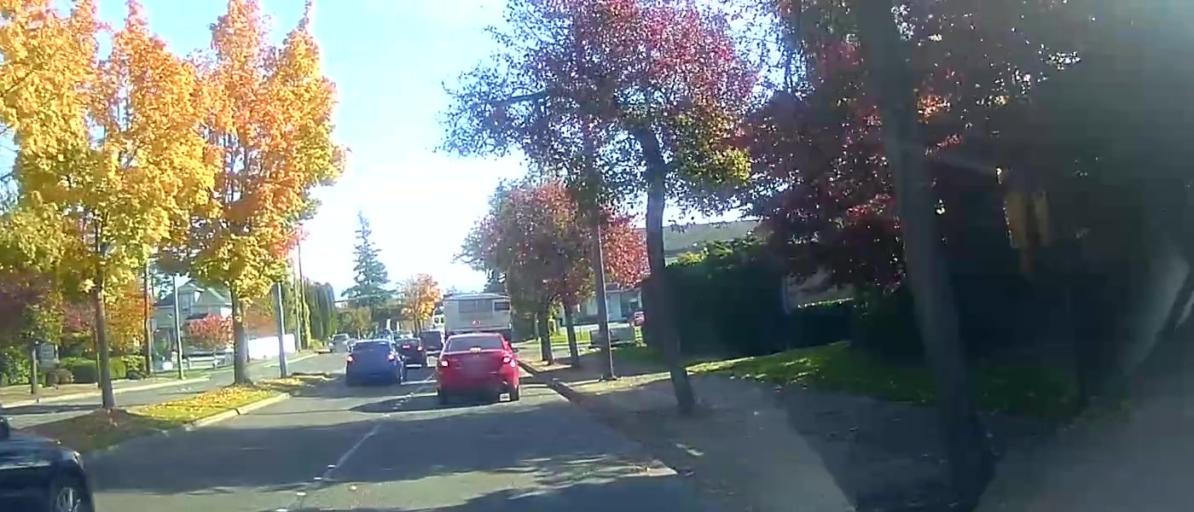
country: US
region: Washington
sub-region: Whatcom County
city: Bellingham
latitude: 48.7449
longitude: -122.4686
